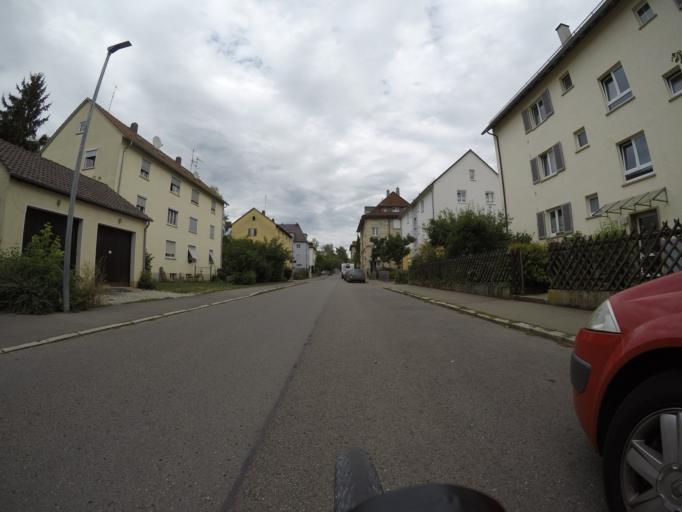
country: DE
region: Baden-Wuerttemberg
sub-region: Tuebingen Region
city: Reutlingen
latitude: 48.4832
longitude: 9.2042
